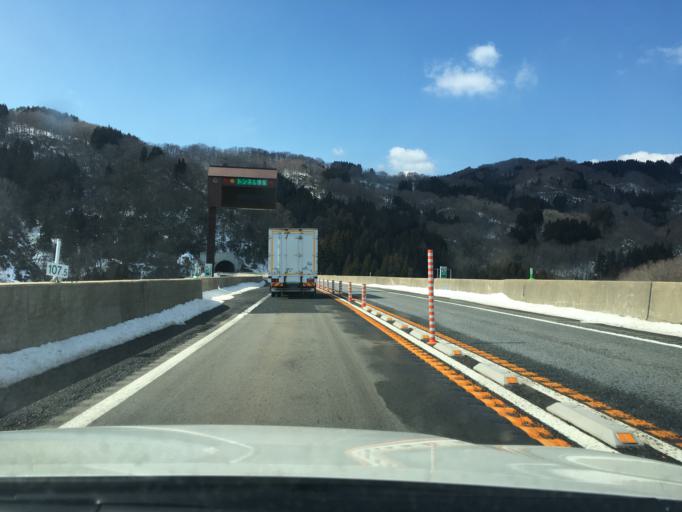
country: JP
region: Yamagata
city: Tsuruoka
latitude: 38.5923
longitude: 139.8847
